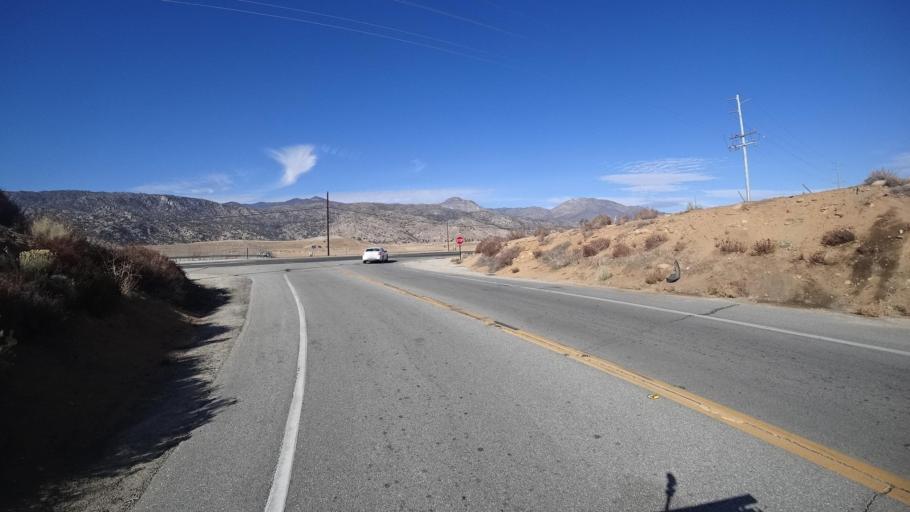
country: US
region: California
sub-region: Kern County
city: Lake Isabella
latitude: 35.6427
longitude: -118.4614
